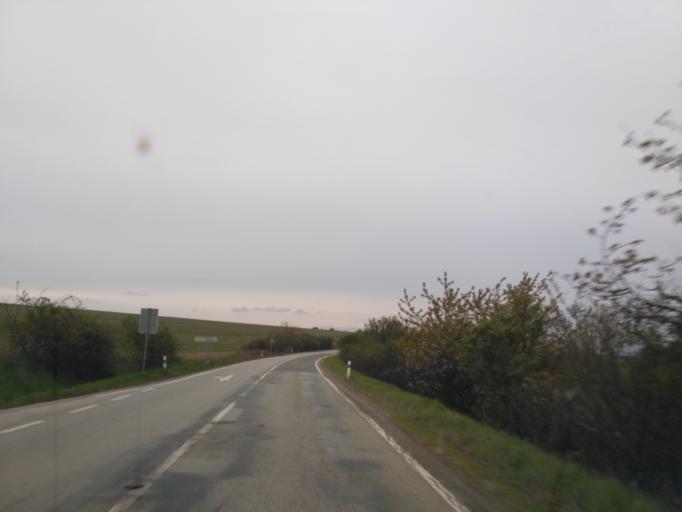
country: SK
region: Kosicky
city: Kosice
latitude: 48.6828
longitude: 21.1963
